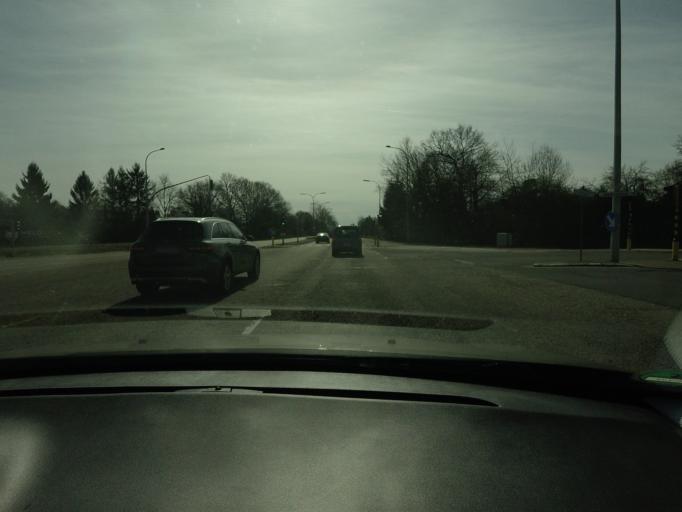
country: BE
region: Flanders
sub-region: Provincie Limburg
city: Zonhoven
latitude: 50.9856
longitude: 5.3590
